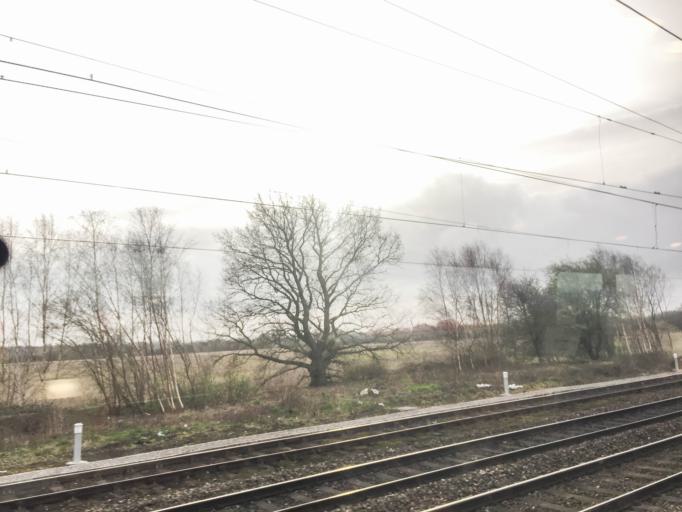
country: GB
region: England
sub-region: Cheshire East
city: Weston
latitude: 53.0749
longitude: -2.4244
